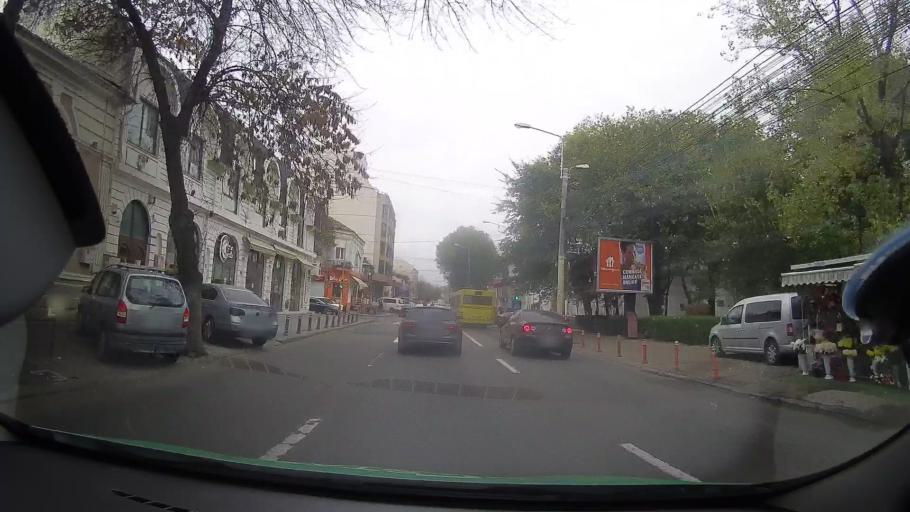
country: RO
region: Constanta
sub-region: Municipiul Constanta
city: Constanta
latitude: 44.1830
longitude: 28.6494
